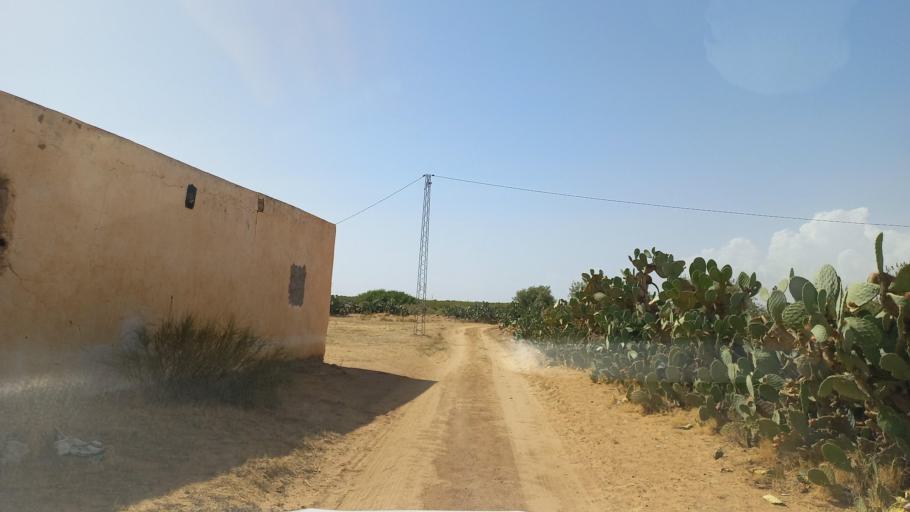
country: TN
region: Al Qasrayn
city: Kasserine
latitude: 35.2108
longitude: 9.0364
